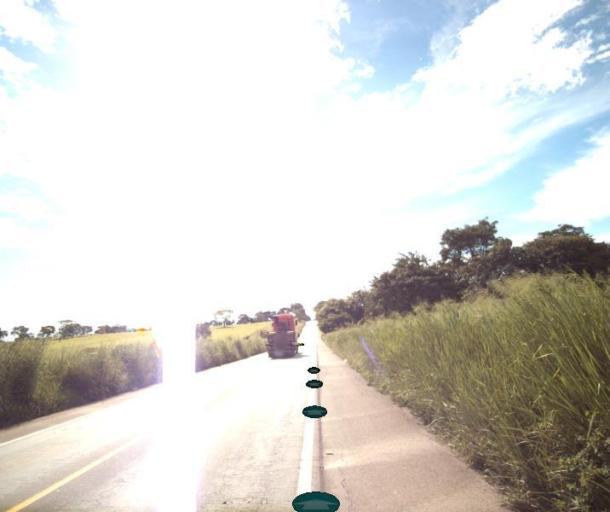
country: BR
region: Goias
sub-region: Jaragua
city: Jaragua
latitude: -15.6177
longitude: -49.3950
